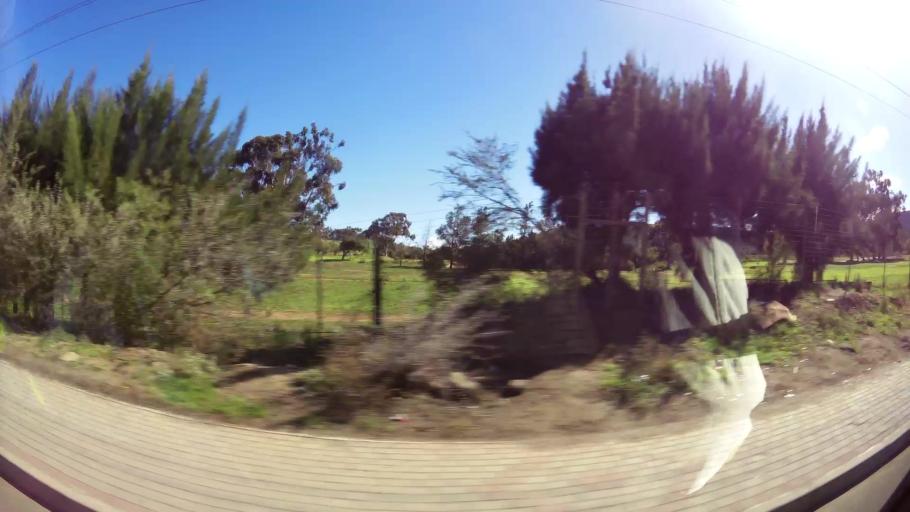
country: ZA
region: Western Cape
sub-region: Cape Winelands District Municipality
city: Ashton
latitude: -33.7735
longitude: 20.1354
